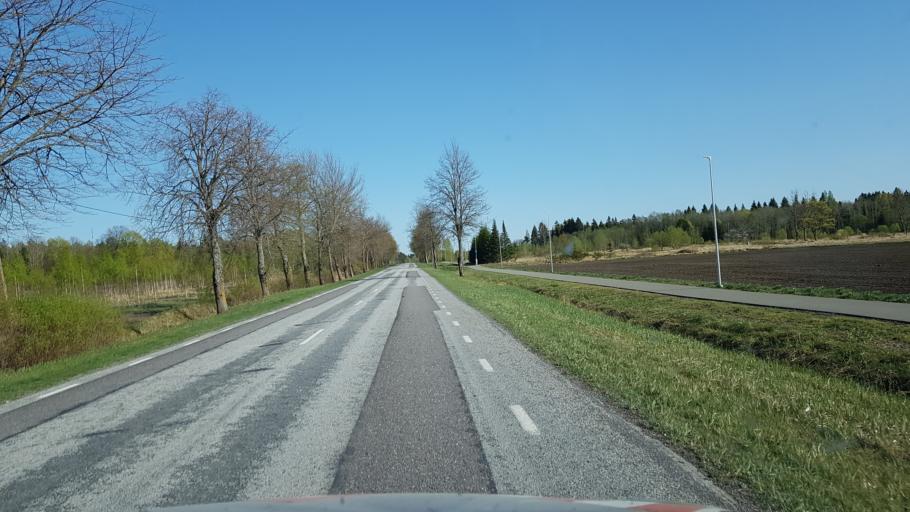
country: EE
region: Paernumaa
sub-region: Paikuse vald
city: Paikuse
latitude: 58.3633
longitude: 24.6477
